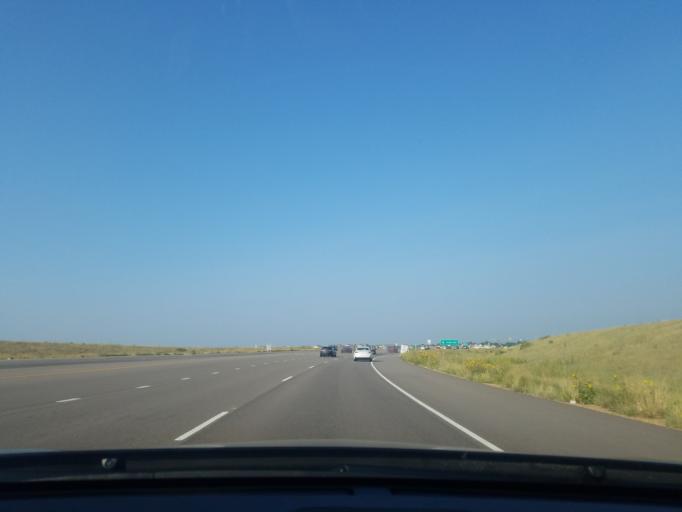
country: US
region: Colorado
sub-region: Larimer County
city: Campion
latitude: 40.3349
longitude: -105.0981
